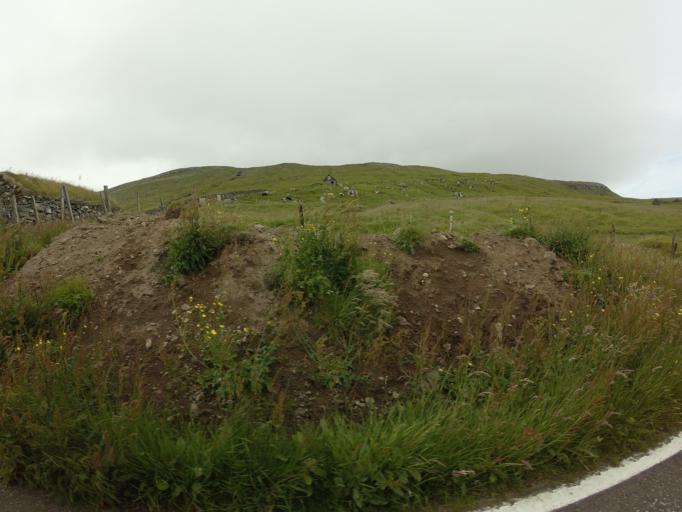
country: FO
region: Sandoy
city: Sandur
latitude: 61.8166
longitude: -6.7096
